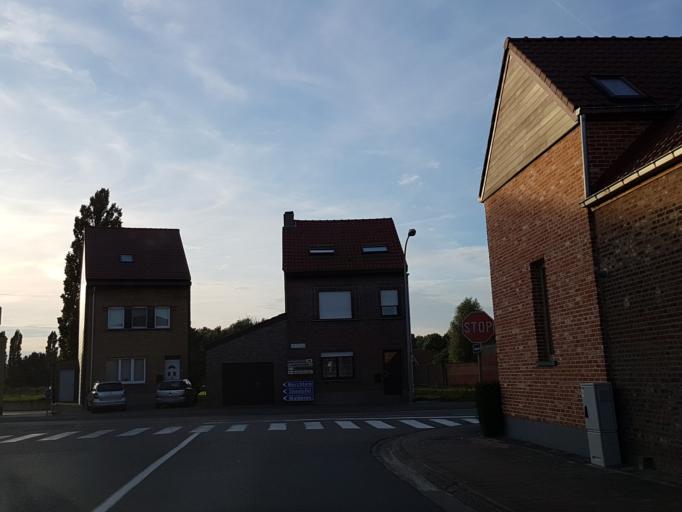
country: BE
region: Flanders
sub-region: Provincie Vlaams-Brabant
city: Londerzeel
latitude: 51.0027
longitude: 4.2955
